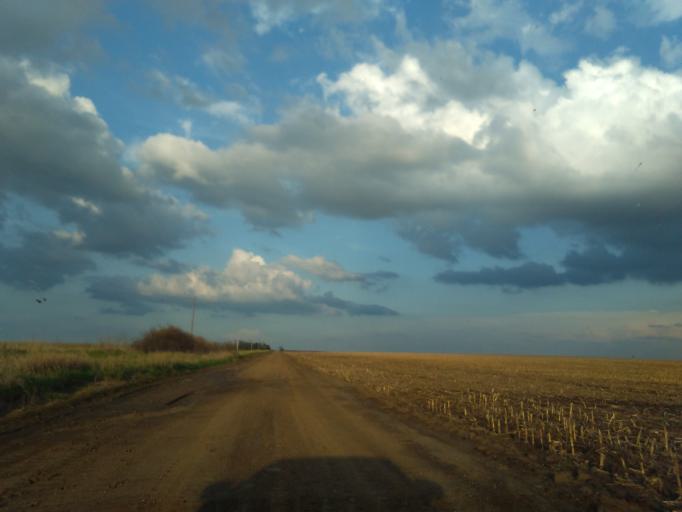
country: US
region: Nebraska
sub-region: Webster County
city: Red Cloud
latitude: 40.2054
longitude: -98.4044
